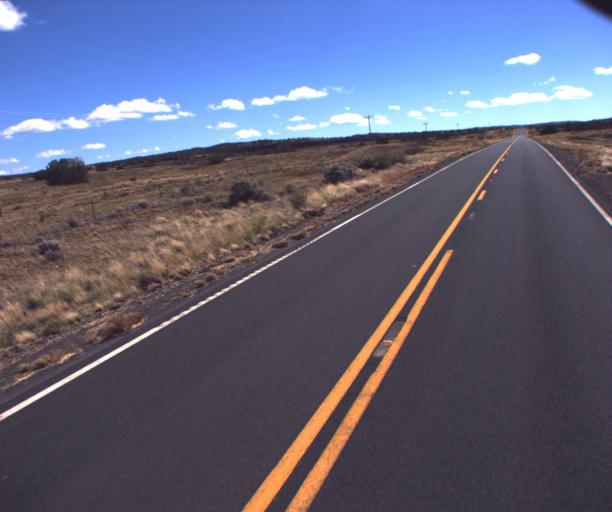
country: US
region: Arizona
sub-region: Apache County
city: Houck
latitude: 35.0822
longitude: -109.3054
